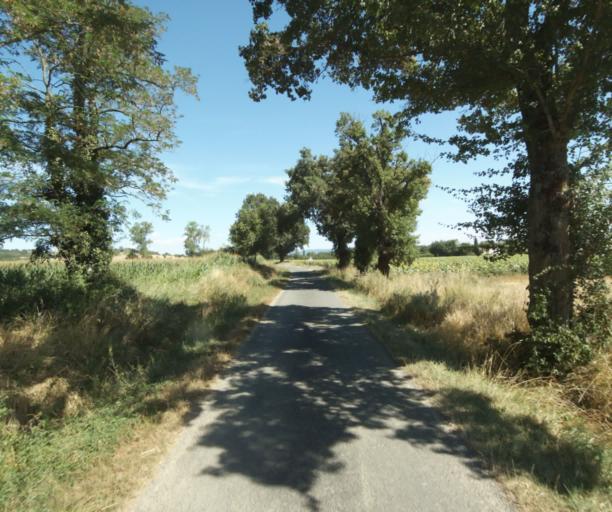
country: FR
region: Midi-Pyrenees
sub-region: Departement de la Haute-Garonne
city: Auriac-sur-Vendinelle
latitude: 43.5192
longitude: 1.8939
